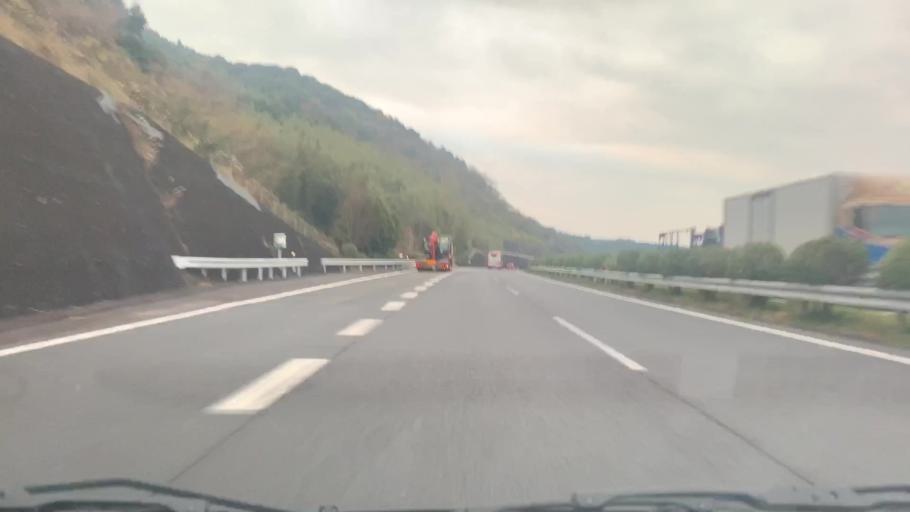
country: JP
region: Nagasaki
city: Omura
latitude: 32.9885
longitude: 129.9579
